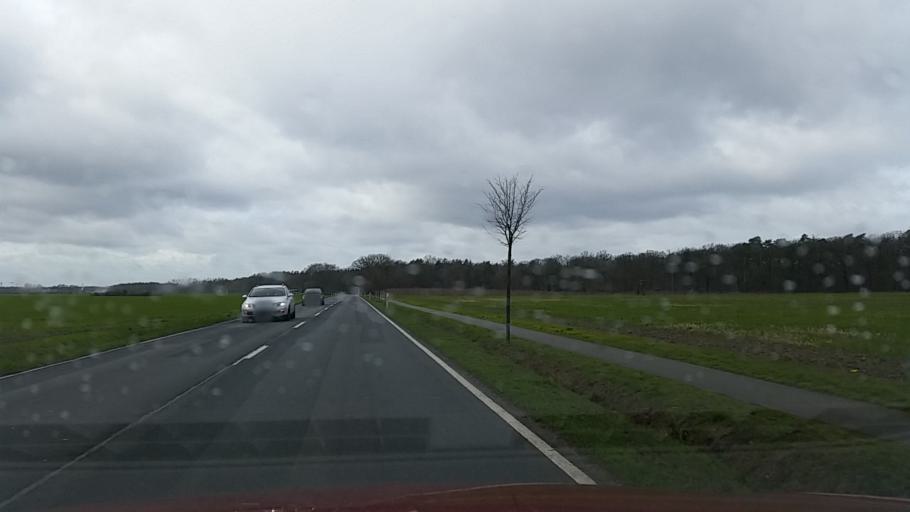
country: DE
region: Lower Saxony
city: Danndorf
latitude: 52.4255
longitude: 10.8985
